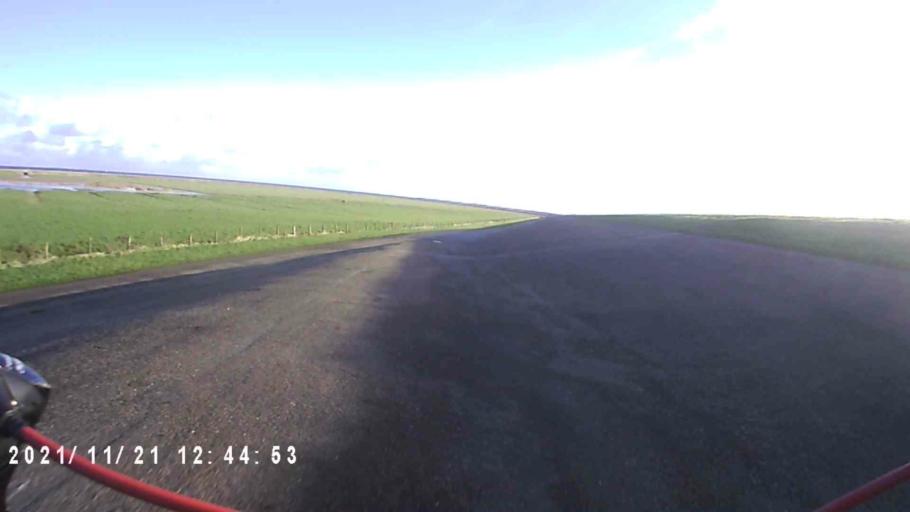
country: NL
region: Friesland
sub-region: Gemeente Dongeradeel
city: Anjum
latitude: 53.4006
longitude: 6.1020
